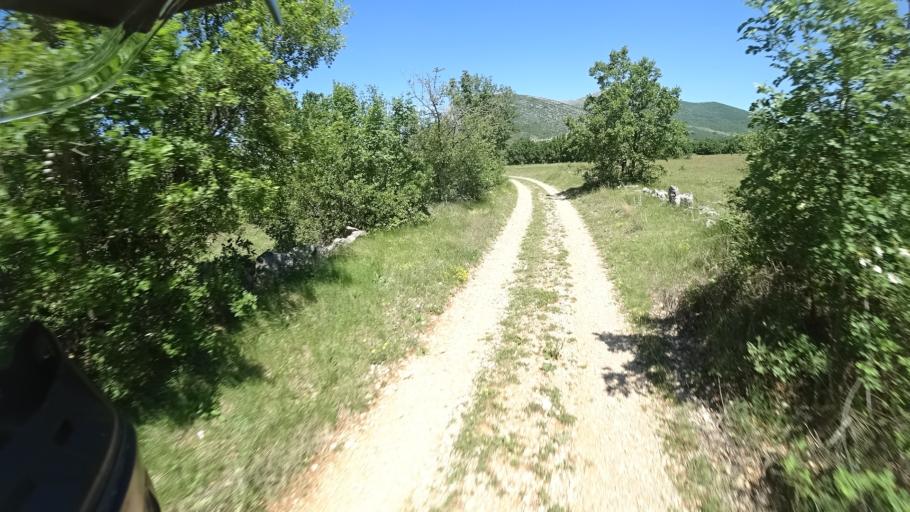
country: BA
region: Federation of Bosnia and Herzegovina
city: Bosansko Grahovo
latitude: 43.9960
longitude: 16.4139
